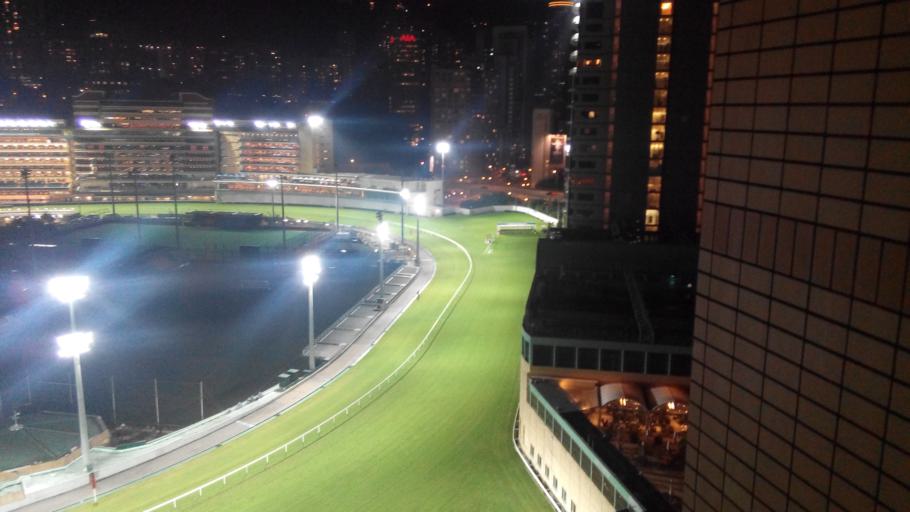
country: HK
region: Wanchai
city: Wan Chai
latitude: 22.2752
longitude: 114.1831
